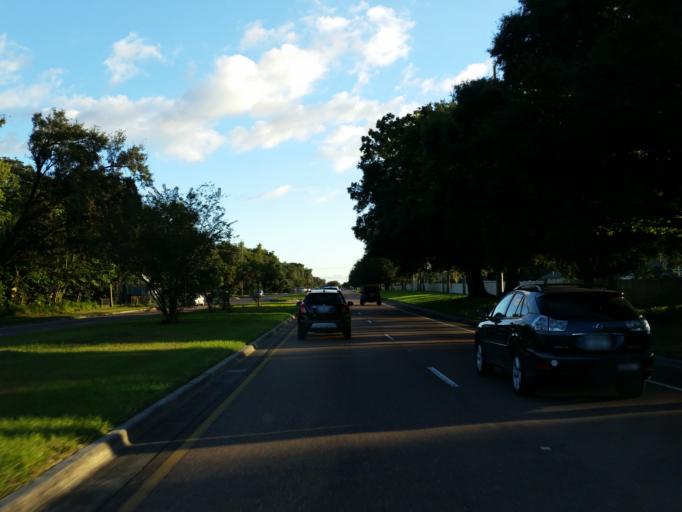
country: US
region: Florida
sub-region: Hillsborough County
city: Riverview
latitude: 27.9054
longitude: -82.3187
